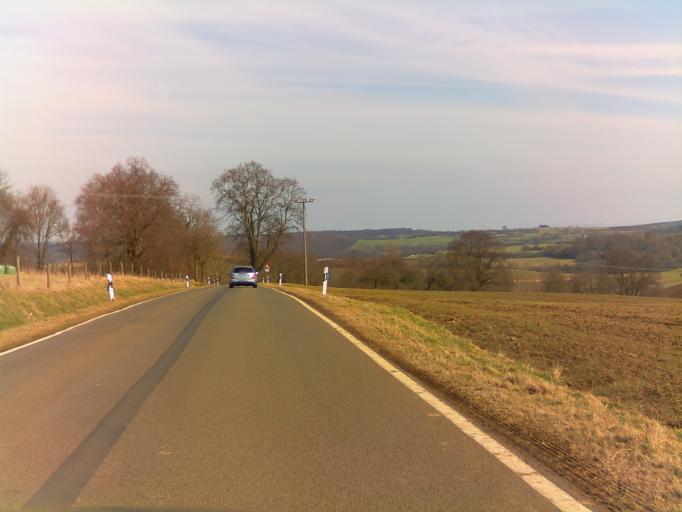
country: DE
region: Hesse
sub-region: Regierungsbezirk Giessen
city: Ulrichstein
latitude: 50.6313
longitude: 9.1430
